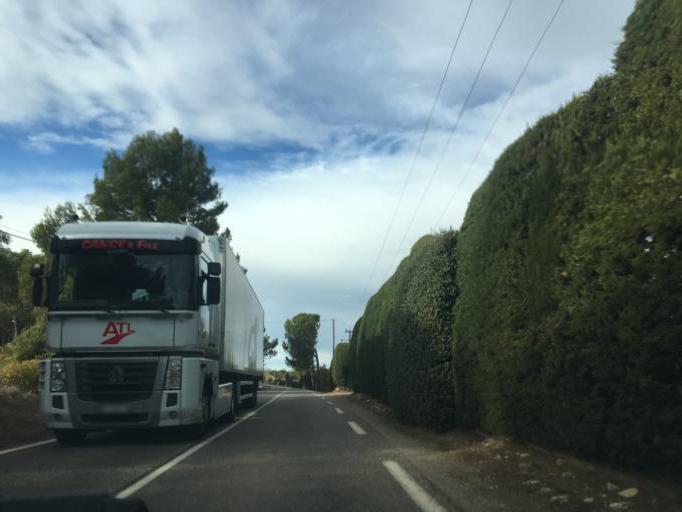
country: FR
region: Provence-Alpes-Cote d'Azur
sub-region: Departement du Var
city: Aups
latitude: 43.6168
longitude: 6.2251
